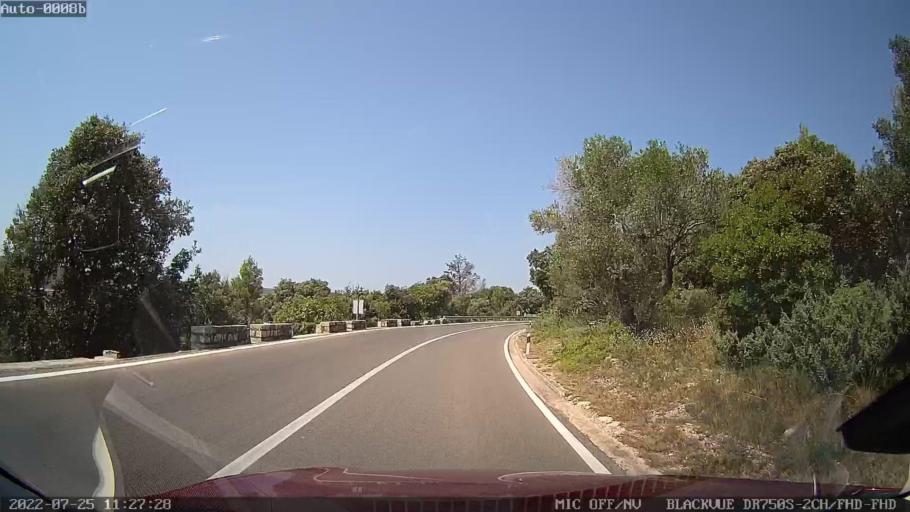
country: HR
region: Zadarska
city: Posedarje
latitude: 44.2131
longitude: 15.4950
